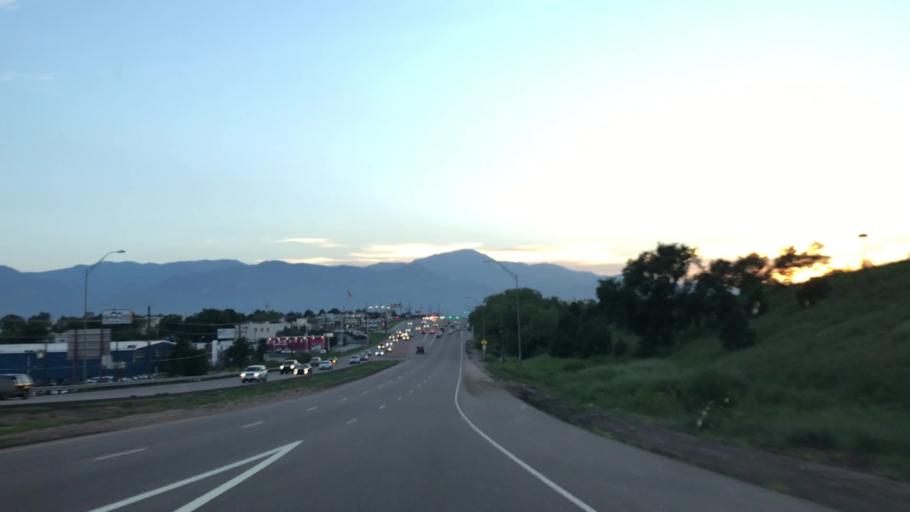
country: US
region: Colorado
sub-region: El Paso County
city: Colorado Springs
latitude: 38.8399
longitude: -104.7617
